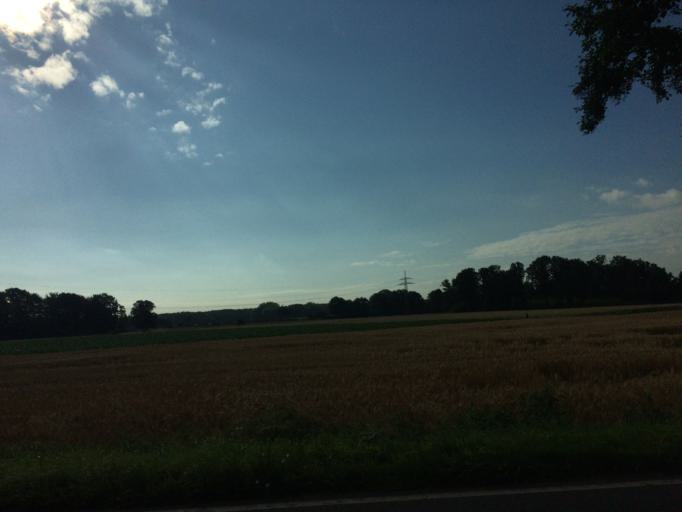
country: DE
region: North Rhine-Westphalia
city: Dorsten
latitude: 51.6867
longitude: 6.9923
